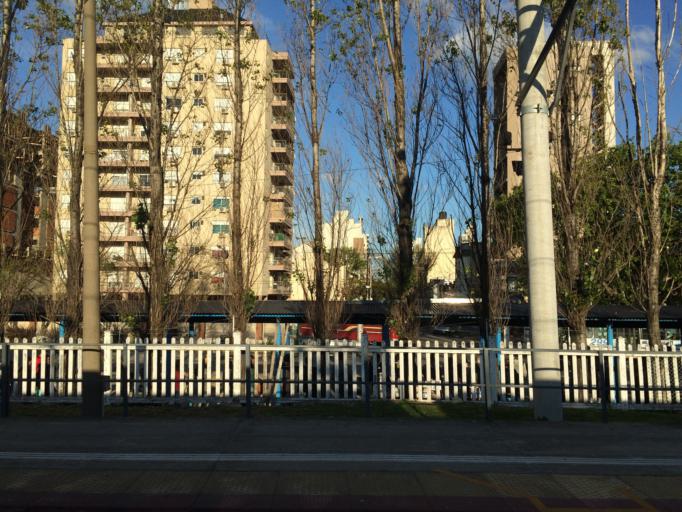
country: AR
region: Buenos Aires
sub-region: Partido de Lomas de Zamora
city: Lomas de Zamora
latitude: -34.7442
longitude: -58.3953
